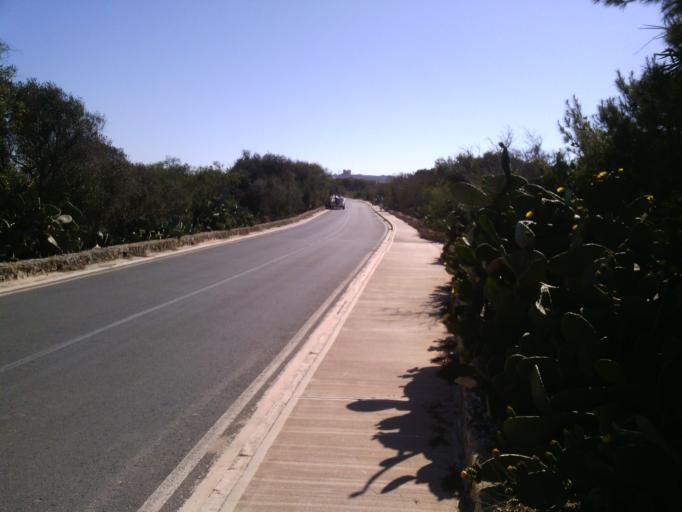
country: MT
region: Il-Mellieha
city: Mellieha
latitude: 35.9833
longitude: 14.3612
